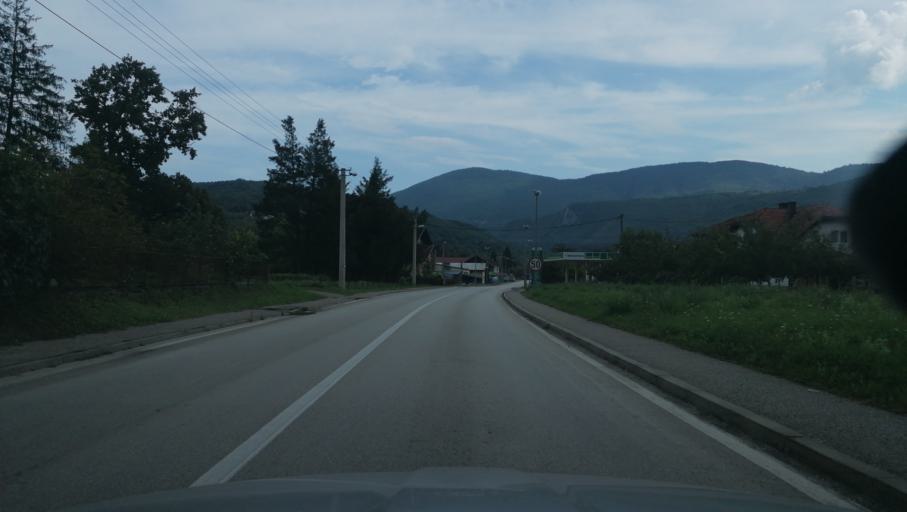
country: BA
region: Republika Srpska
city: Hiseti
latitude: 44.6144
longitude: 17.1426
